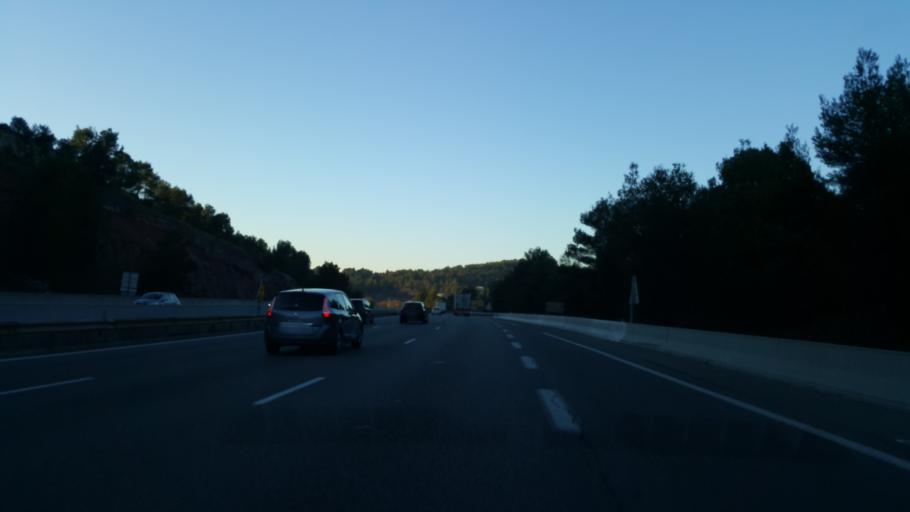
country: FR
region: Provence-Alpes-Cote d'Azur
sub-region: Departement des Bouches-du-Rhone
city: Le Tholonet
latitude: 43.4995
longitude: 5.5230
